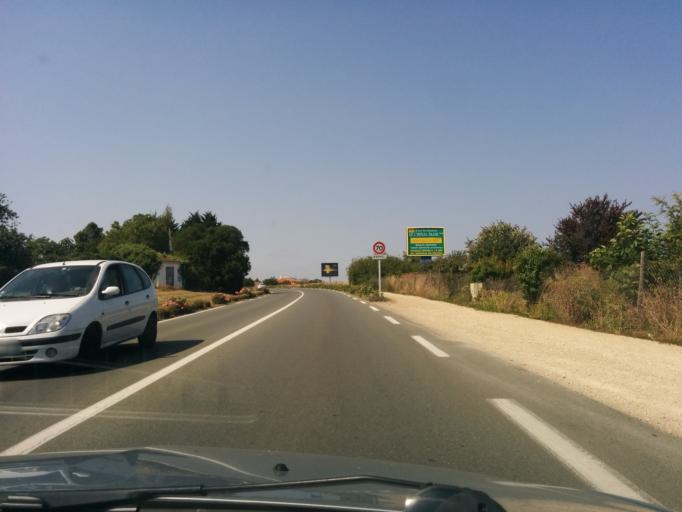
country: FR
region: Poitou-Charentes
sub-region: Departement de la Vienne
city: Jaunay-Clan
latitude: 46.6767
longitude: 0.3657
